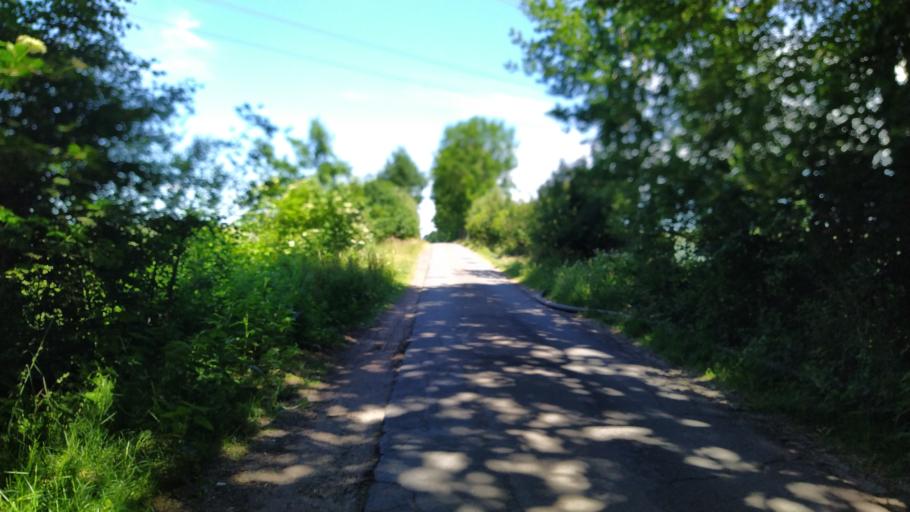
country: DE
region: Lower Saxony
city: Deinste
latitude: 53.5083
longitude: 9.4405
